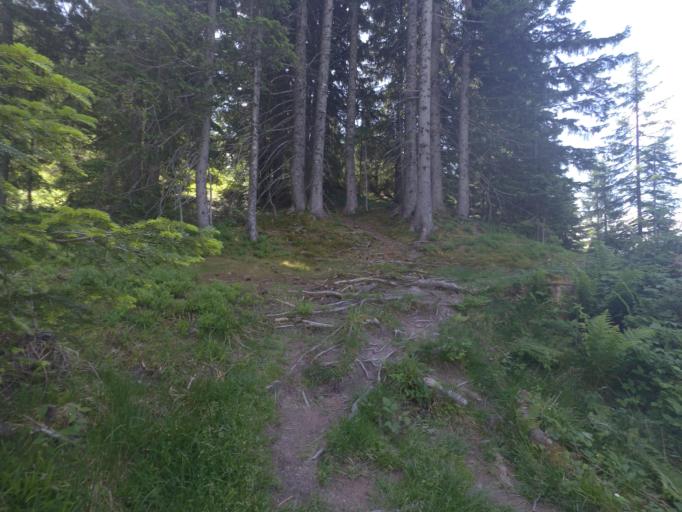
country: AT
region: Salzburg
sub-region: Politischer Bezirk Zell am See
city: Dienten am Hochkonig
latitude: 47.4141
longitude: 13.0002
